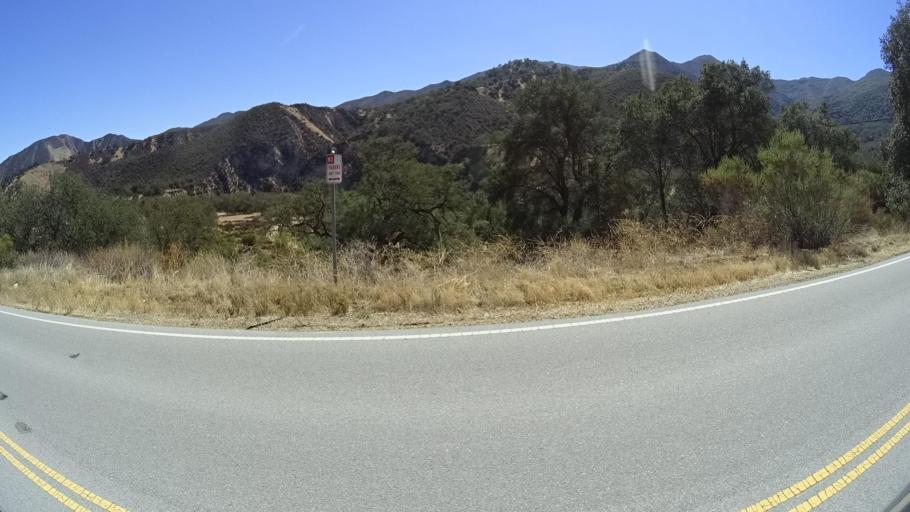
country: US
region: California
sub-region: Monterey County
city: Greenfield
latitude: 36.2369
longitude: -121.4512
